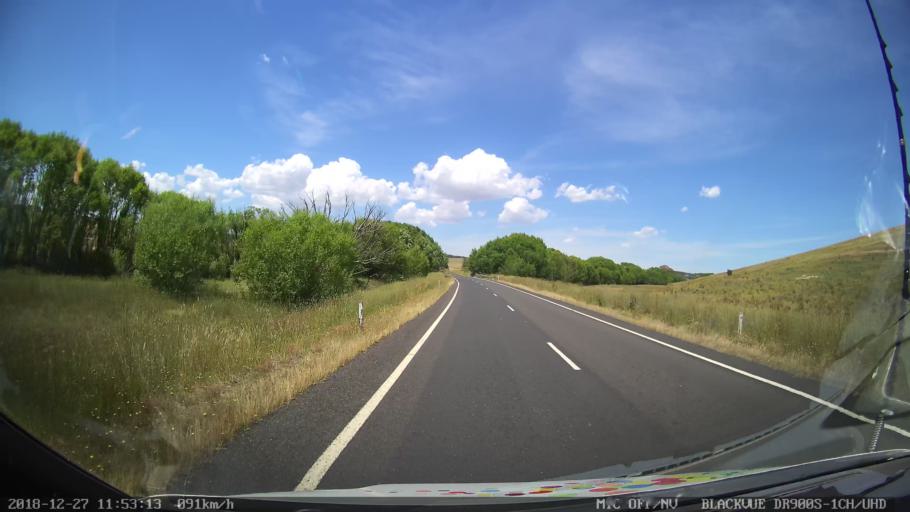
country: AU
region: New South Wales
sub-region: Blayney
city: Blayney
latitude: -33.6590
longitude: 149.4025
